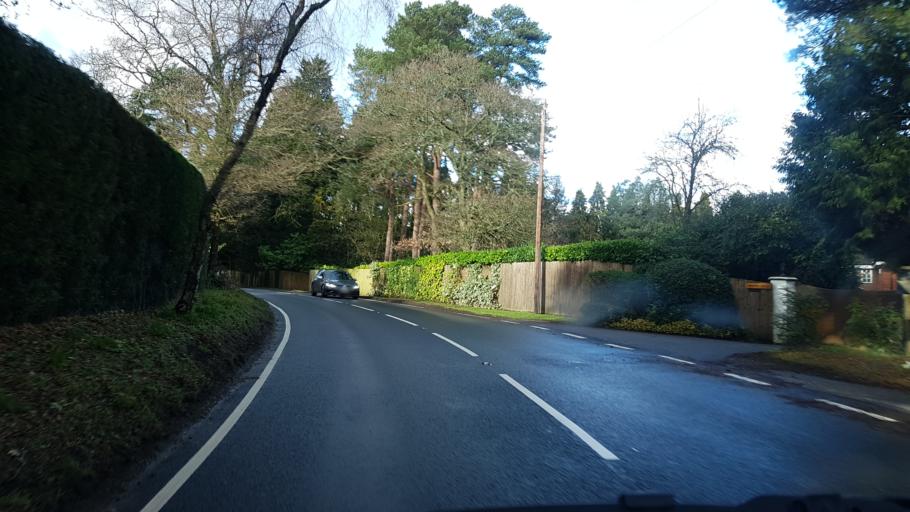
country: GB
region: England
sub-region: Surrey
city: Elstead
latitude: 51.1762
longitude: -0.7482
